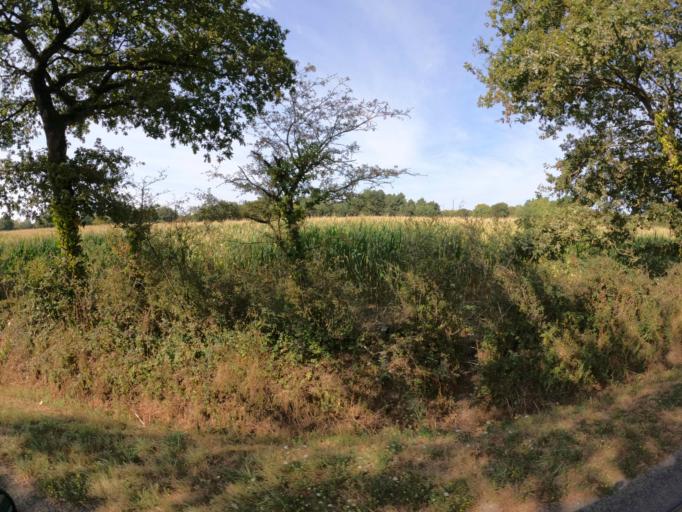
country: FR
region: Pays de la Loire
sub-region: Departement de la Vendee
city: Saint-Christophe-du-Ligneron
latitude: 46.8108
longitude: -1.8082
